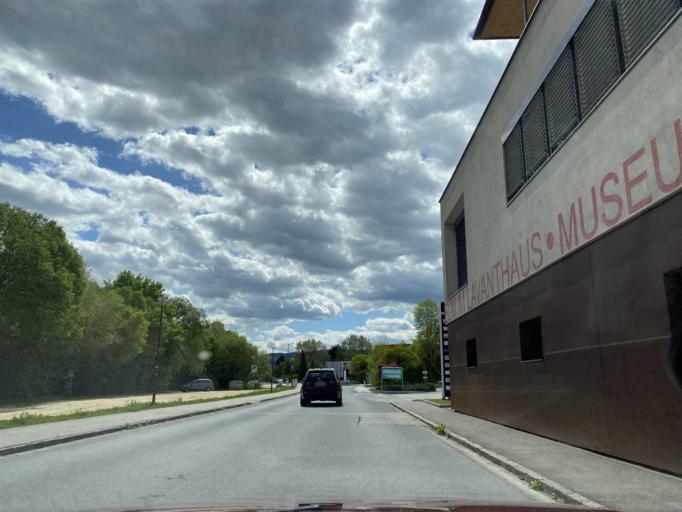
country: AT
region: Carinthia
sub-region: Politischer Bezirk Wolfsberg
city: Wolfsberg
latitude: 46.8363
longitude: 14.8412
